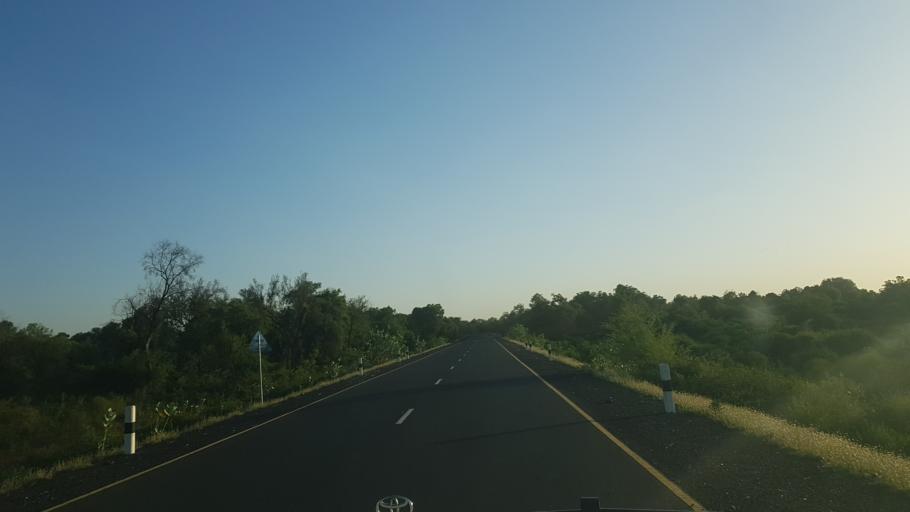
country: ET
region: Southern Nations, Nationalities, and People's Region
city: Lobuni
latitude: 5.1711
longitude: 36.0882
